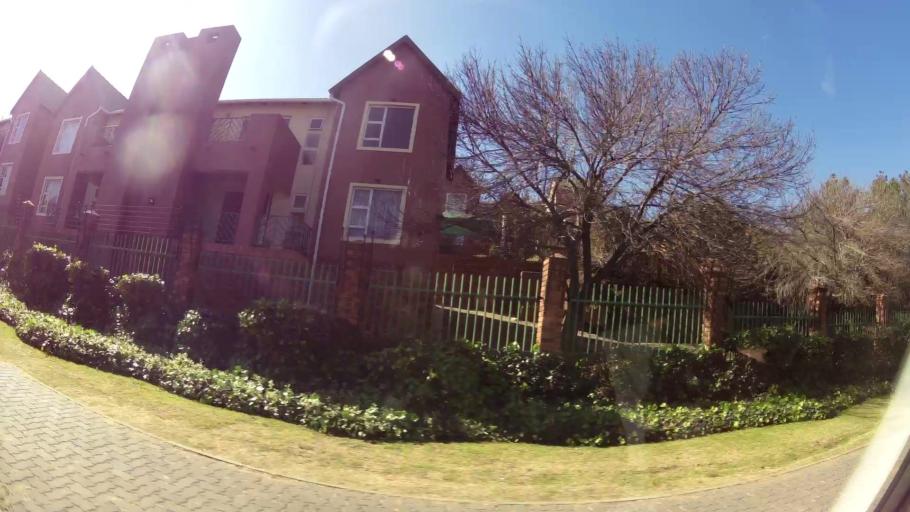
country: ZA
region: Gauteng
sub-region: City of Johannesburg Metropolitan Municipality
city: Johannesburg
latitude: -26.2684
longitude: 28.0189
